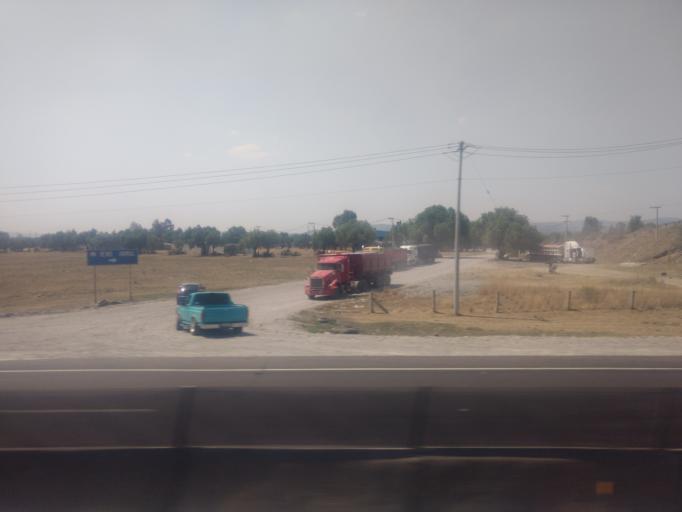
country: MX
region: Morelos
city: San Martin de las Piramides
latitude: 19.6747
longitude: -98.8236
